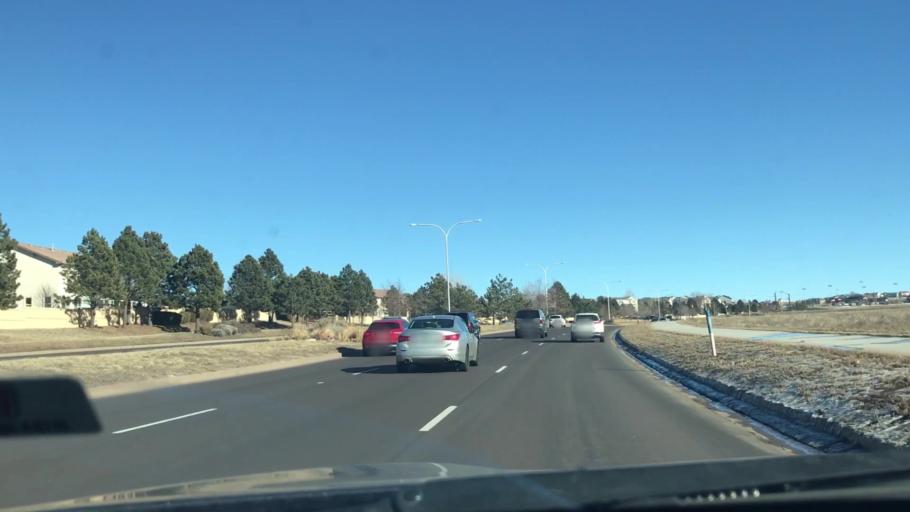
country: US
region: Colorado
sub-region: El Paso County
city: Black Forest
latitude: 38.9679
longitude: -104.7721
